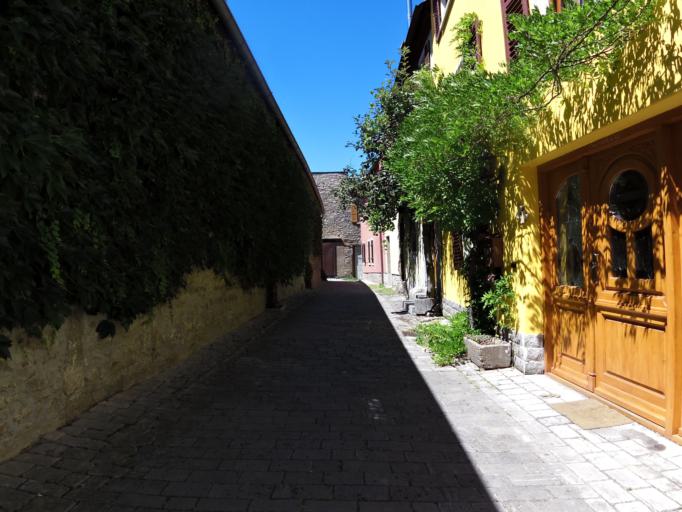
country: DE
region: Bavaria
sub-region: Regierungsbezirk Unterfranken
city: Ochsenfurt
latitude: 49.6656
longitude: 10.0654
